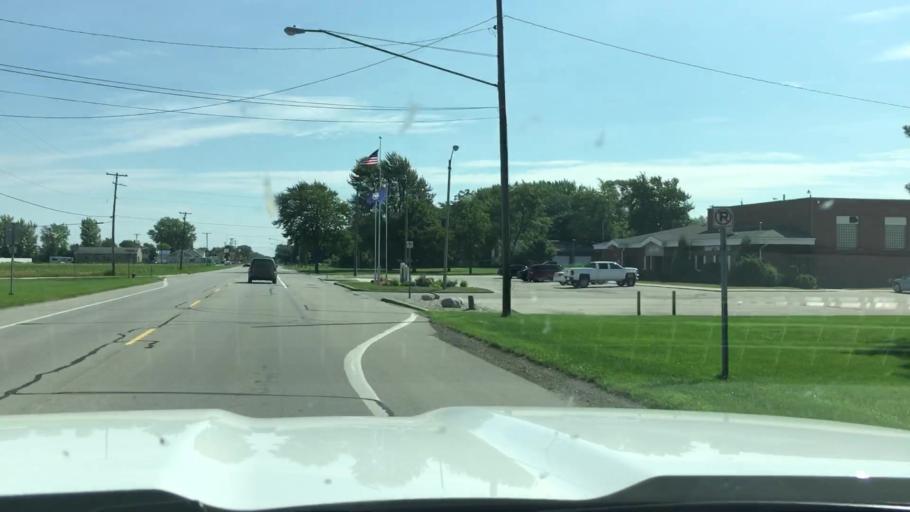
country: US
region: Michigan
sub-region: Bay County
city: Essexville
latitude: 43.5941
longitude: -83.8106
